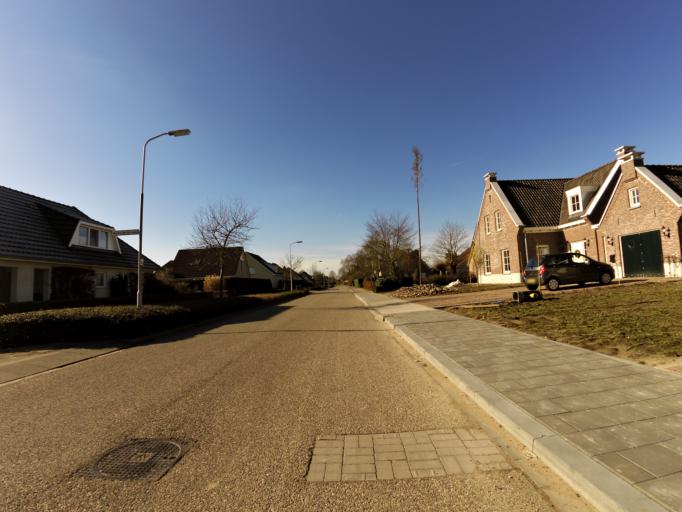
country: NL
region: Gelderland
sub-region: Gemeente Doesburg
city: Doesburg
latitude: 51.9421
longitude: 6.1443
